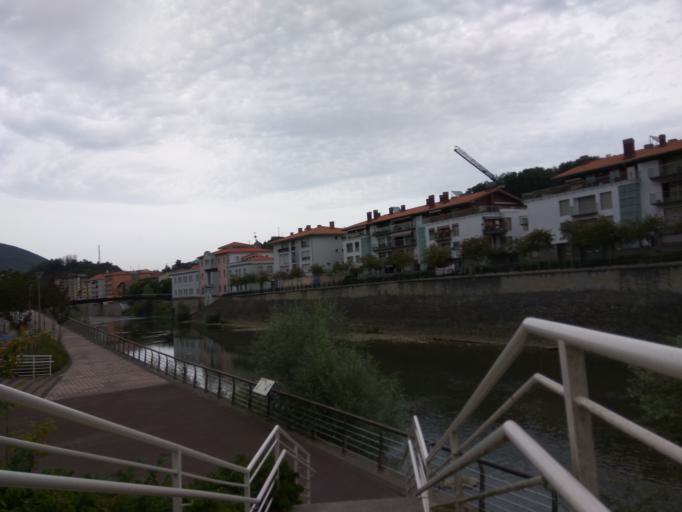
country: ES
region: Basque Country
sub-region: Provincia de Guipuzcoa
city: Villabona
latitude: 43.1865
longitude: -2.0549
